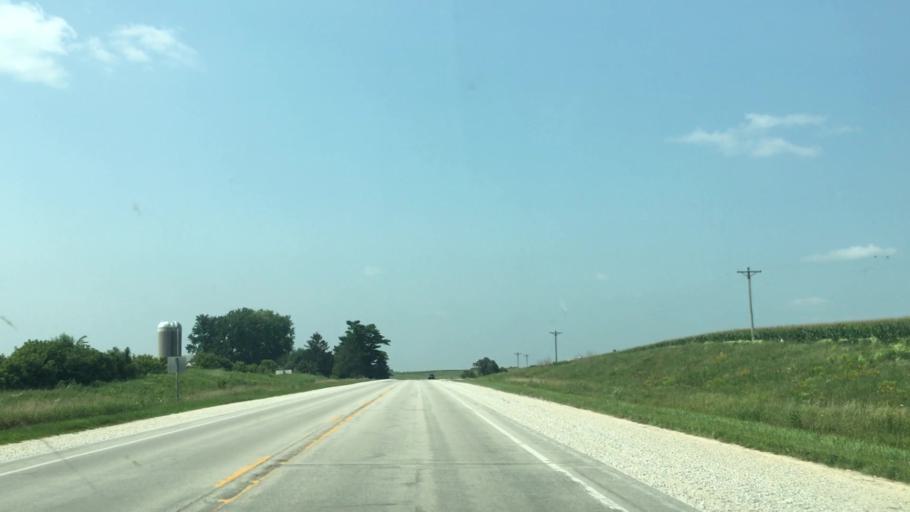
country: US
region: Iowa
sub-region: Winneshiek County
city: Decorah
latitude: 43.4112
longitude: -91.8573
